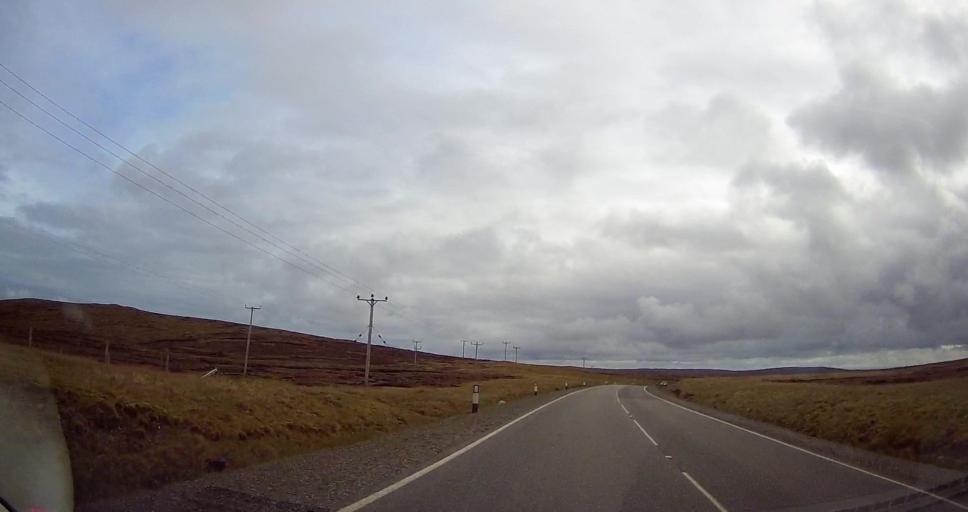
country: GB
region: Scotland
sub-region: Shetland Islands
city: Shetland
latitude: 60.5895
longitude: -1.1687
